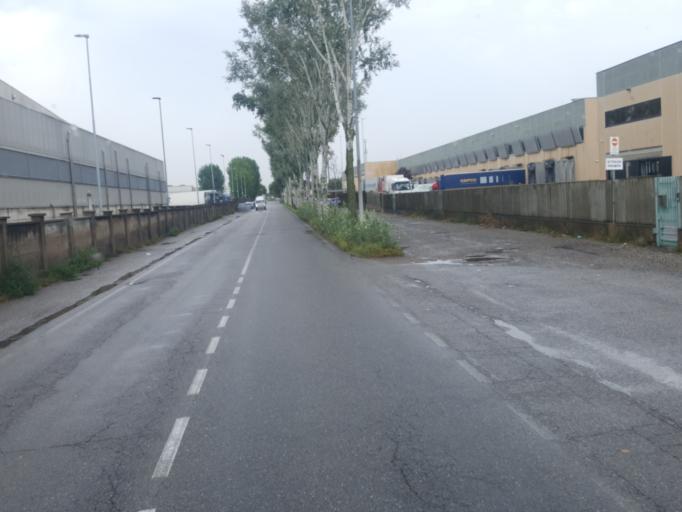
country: IT
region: Lombardy
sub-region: Provincia di Varese
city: Origgio
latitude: 45.5921
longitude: 9.0263
